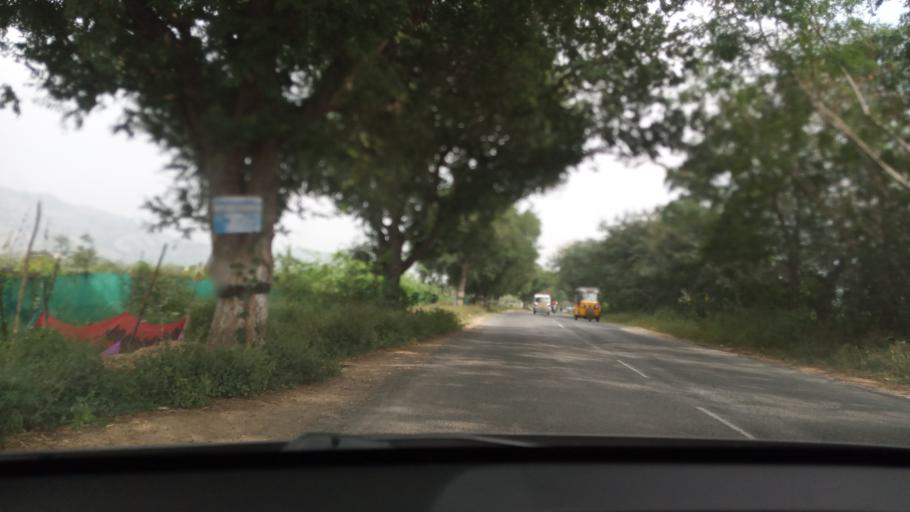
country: IN
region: Andhra Pradesh
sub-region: Chittoor
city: Madanapalle
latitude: 13.6518
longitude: 78.8191
